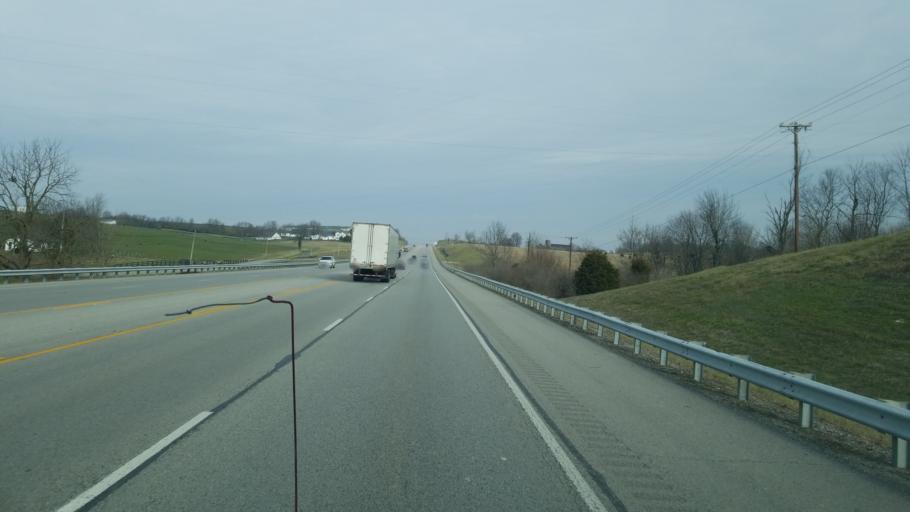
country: US
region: Kentucky
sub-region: Boyle County
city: Junction City
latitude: 37.6032
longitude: -84.7736
